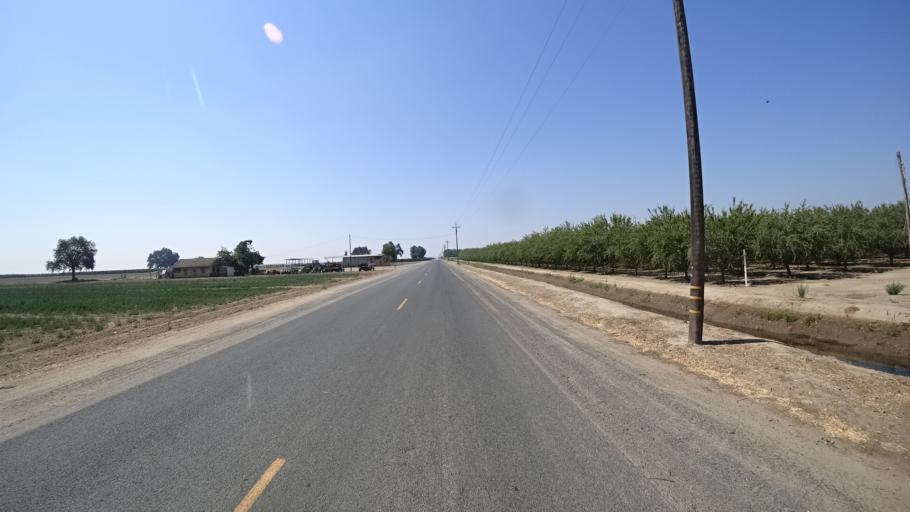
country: US
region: California
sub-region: Fresno County
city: Kingsburg
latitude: 36.4553
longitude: -119.5284
